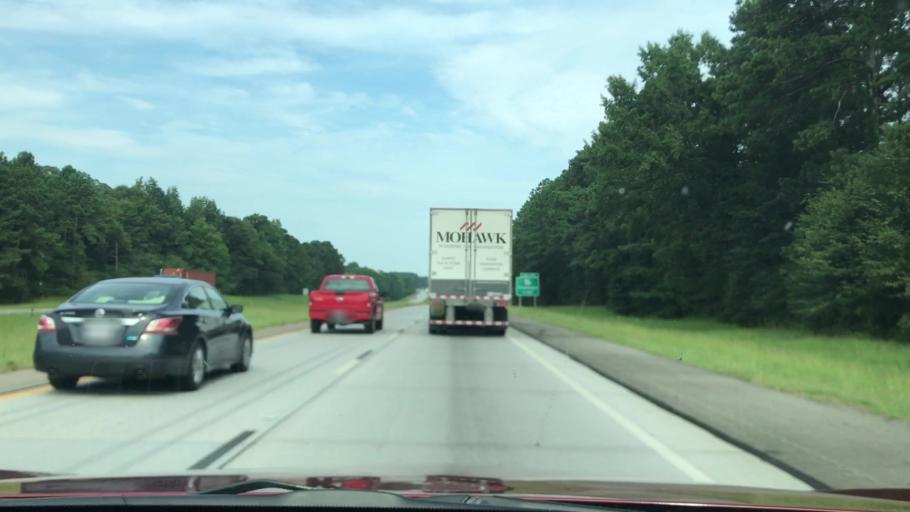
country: US
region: Georgia
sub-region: McDuffie County
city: Thomson
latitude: 33.5097
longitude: -82.4304
